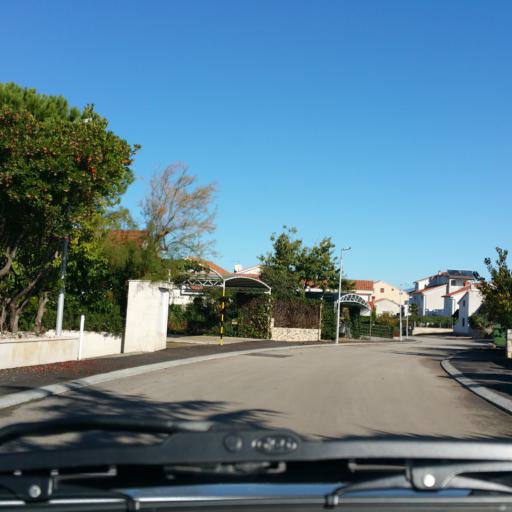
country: HR
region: Primorsko-Goranska
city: Njivice
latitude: 45.1501
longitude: 14.5404
